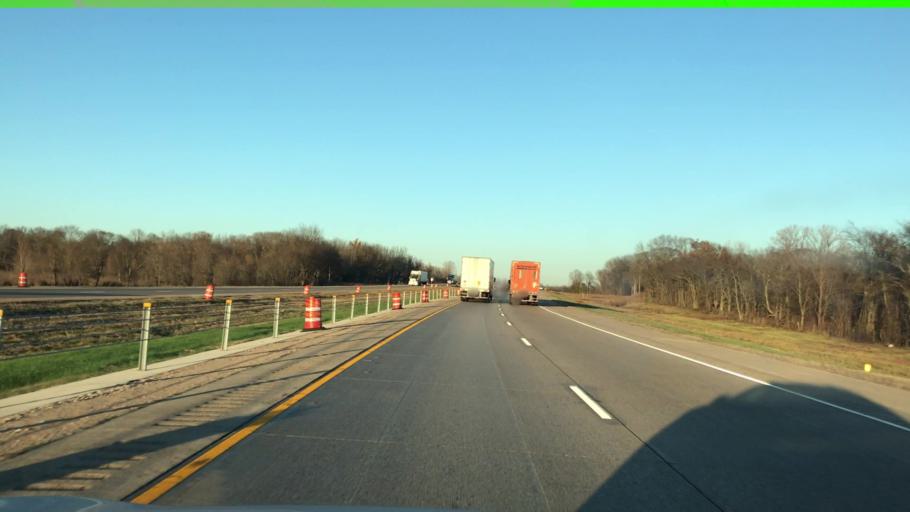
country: US
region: Arkansas
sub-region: Miller County
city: Texarkana
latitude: 33.5856
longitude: -93.8399
